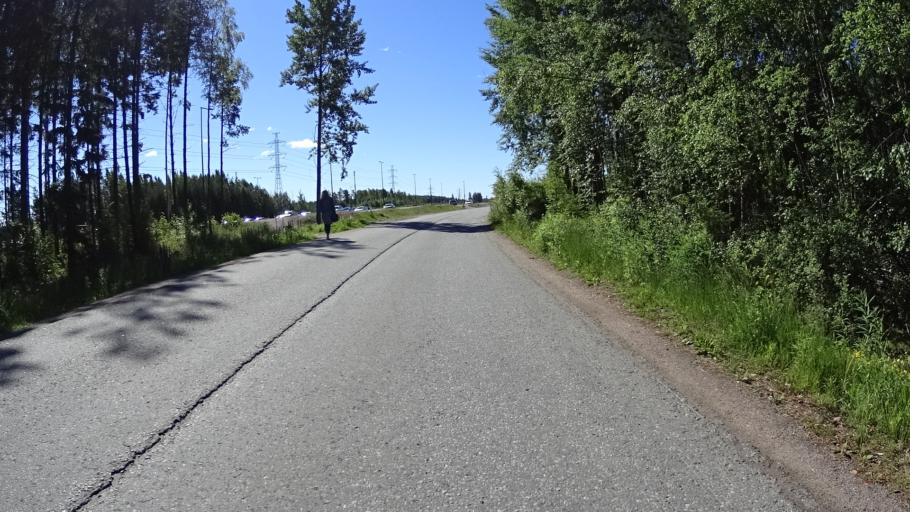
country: FI
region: Uusimaa
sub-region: Helsinki
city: Kilo
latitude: 60.3132
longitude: 24.8375
